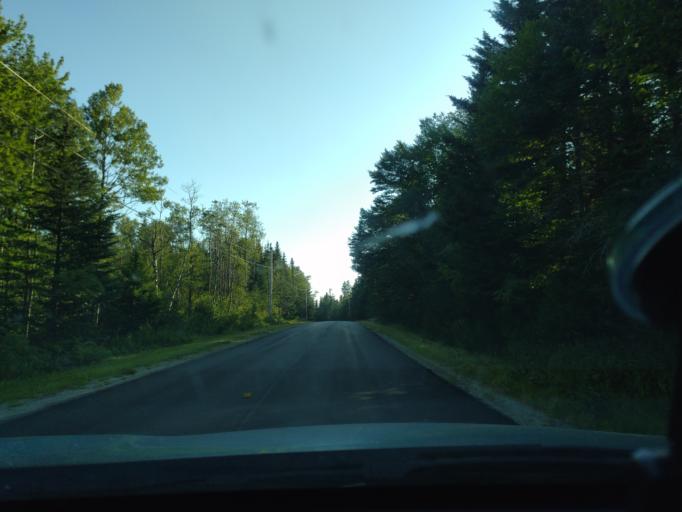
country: US
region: Maine
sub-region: Washington County
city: East Machias
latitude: 44.7016
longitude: -67.1545
